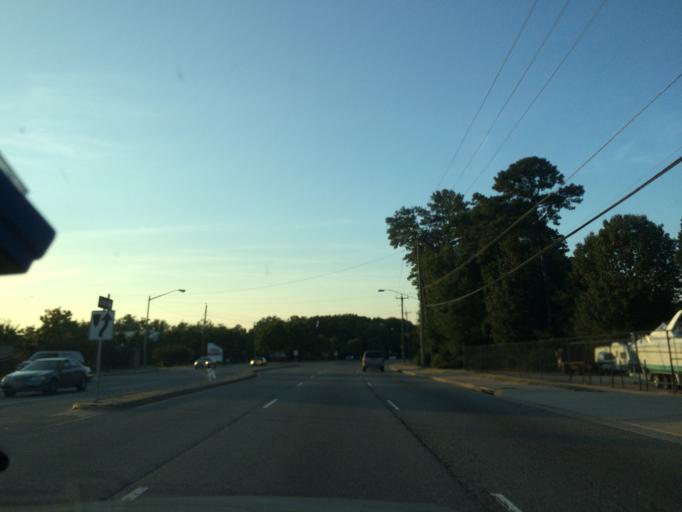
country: US
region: Virginia
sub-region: City of Newport News
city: Newport News
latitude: 37.0421
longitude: -76.4587
